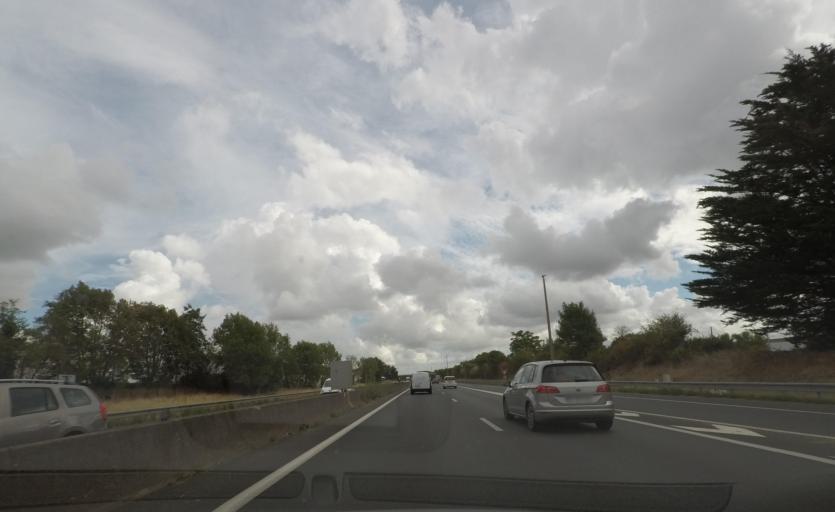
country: FR
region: Pays de la Loire
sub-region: Departement de Maine-et-Loire
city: Angers
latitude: 47.4740
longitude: -0.5061
